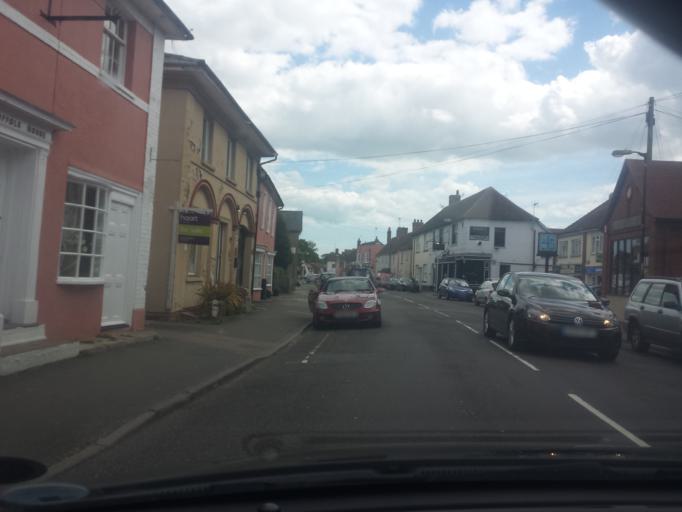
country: GB
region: England
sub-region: Essex
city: Little Clacton
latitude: 51.8581
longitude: 1.1613
